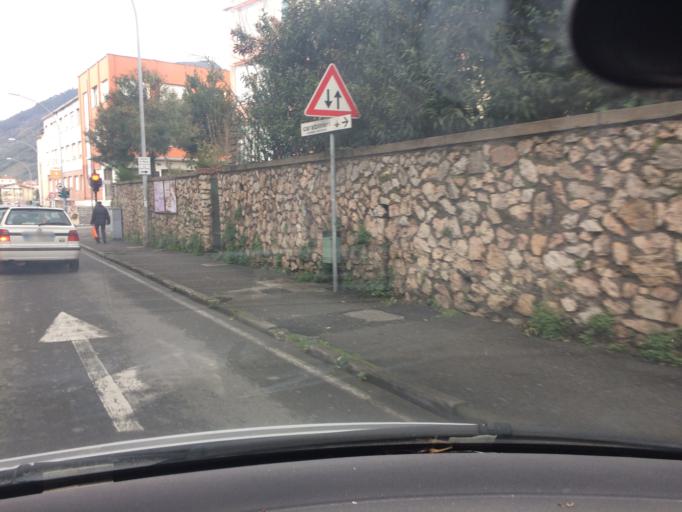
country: IT
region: Tuscany
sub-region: Provincia di Massa-Carrara
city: Massa
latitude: 44.0388
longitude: 10.1400
